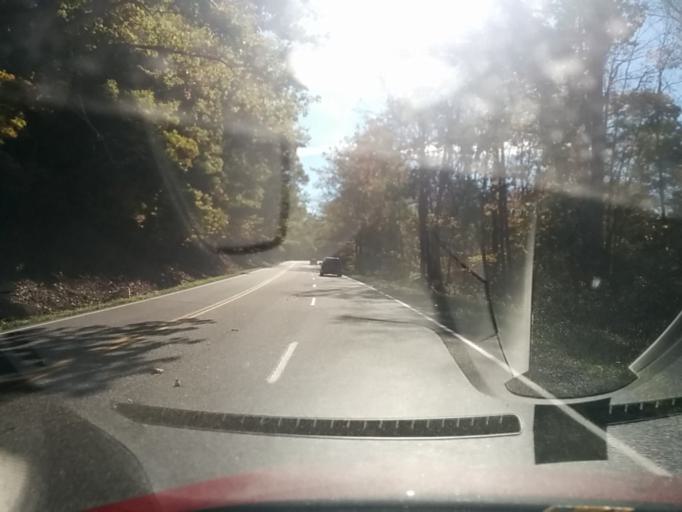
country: US
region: Virginia
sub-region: City of Lexington
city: Lexington
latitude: 37.7105
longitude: -79.4689
